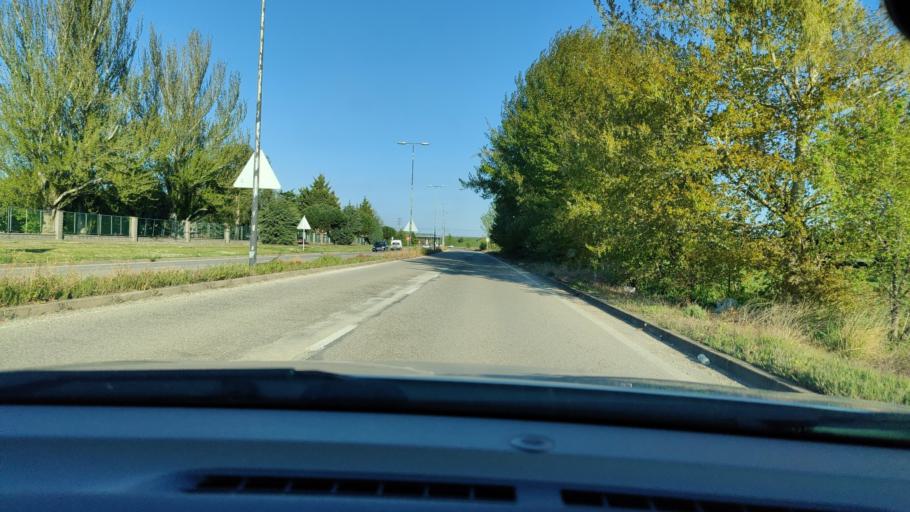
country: ES
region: Castille and Leon
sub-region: Provincia de Burgos
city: Villalbilla de Burgos
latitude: 42.3590
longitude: -3.7672
